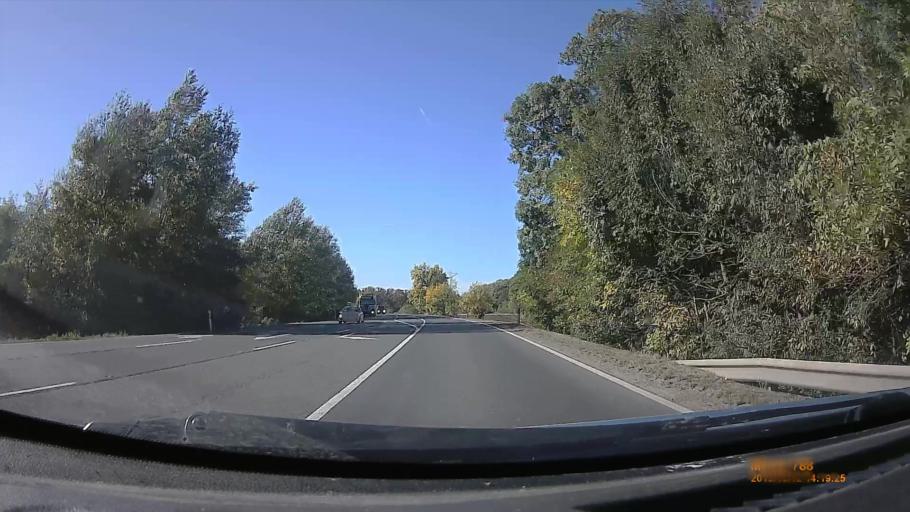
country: HU
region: Hajdu-Bihar
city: Biharkeresztes
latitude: 47.1276
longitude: 21.7646
